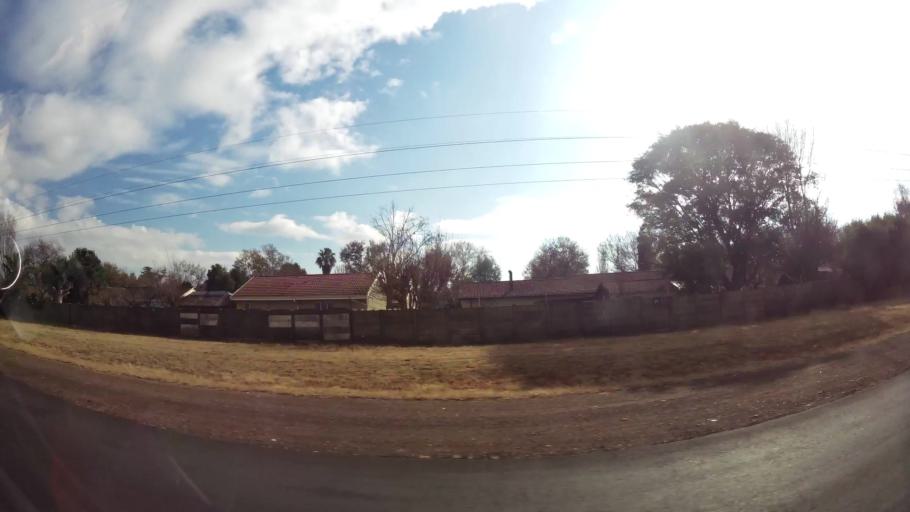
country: ZA
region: Gauteng
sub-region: Sedibeng District Municipality
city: Meyerton
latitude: -26.5570
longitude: 28.0378
